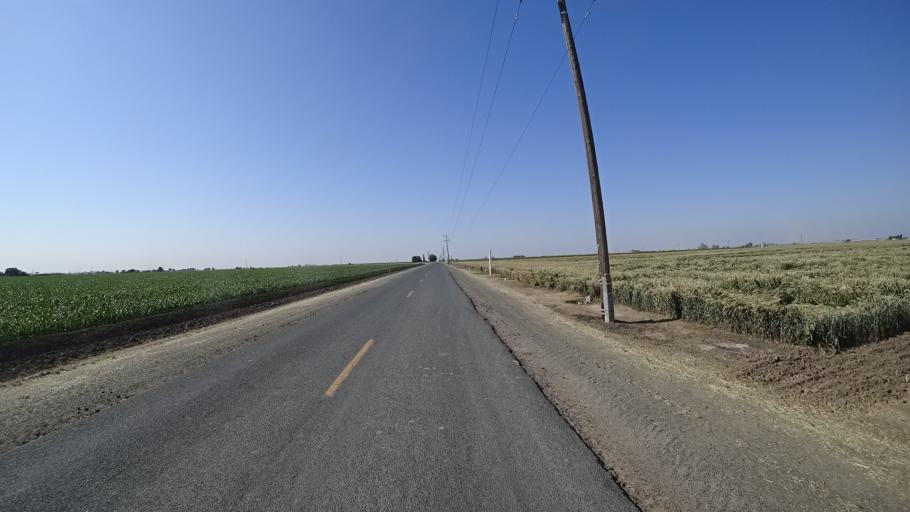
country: US
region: California
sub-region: Kings County
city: Home Garden
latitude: 36.2438
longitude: -119.5831
